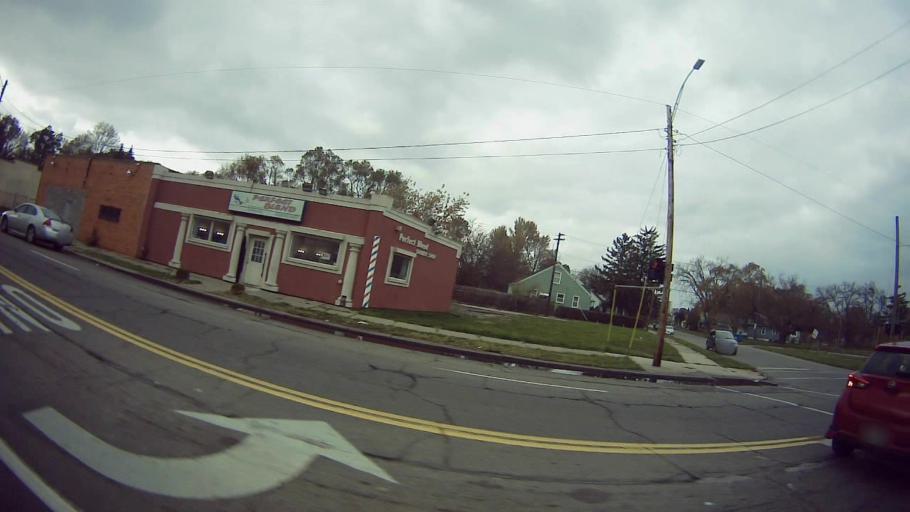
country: US
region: Michigan
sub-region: Macomb County
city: Eastpointe
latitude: 42.4233
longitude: -82.9945
